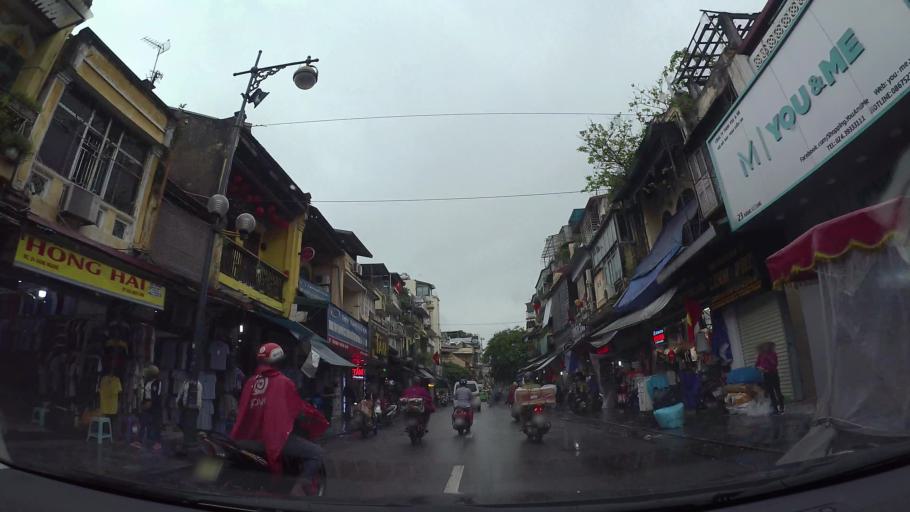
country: VN
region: Ha Noi
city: Hoan Kiem
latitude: 21.0349
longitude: 105.8505
